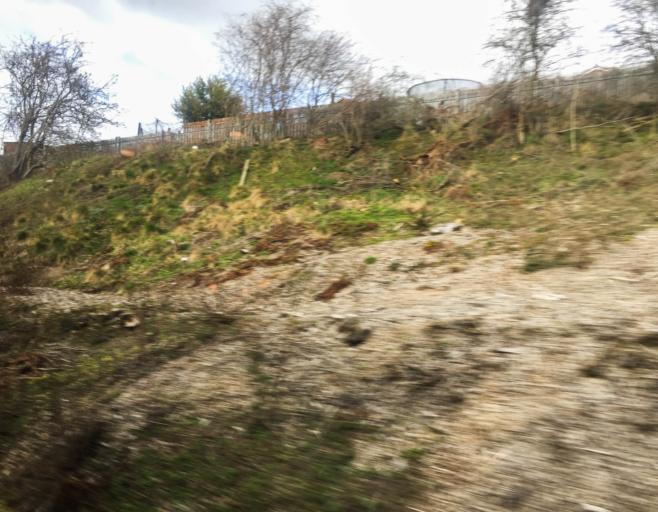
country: GB
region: Scotland
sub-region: North Lanarkshire
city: Wishaw
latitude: 55.7666
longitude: -3.9163
